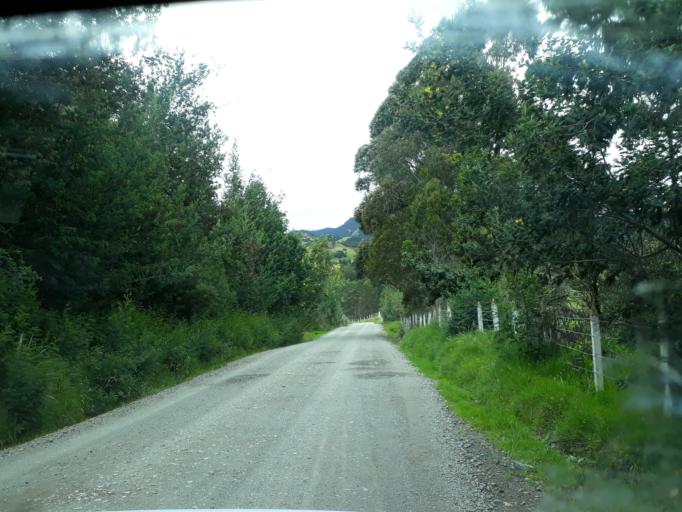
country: CO
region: Cundinamarca
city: La Mesa
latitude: 5.2877
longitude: -73.9066
